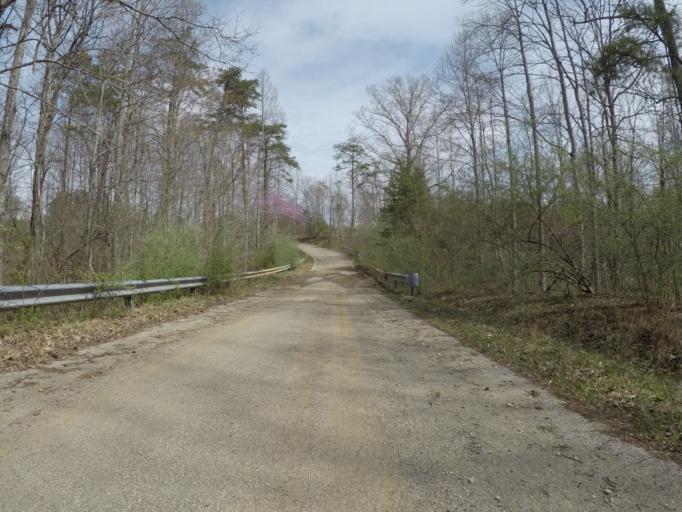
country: US
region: West Virginia
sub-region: Cabell County
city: Pea Ridge
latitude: 38.3240
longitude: -82.3507
